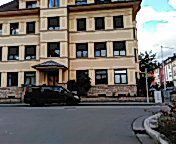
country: LU
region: Luxembourg
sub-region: Canton d'Esch-sur-Alzette
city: Esch-sur-Alzette
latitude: 49.5007
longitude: 5.9740
